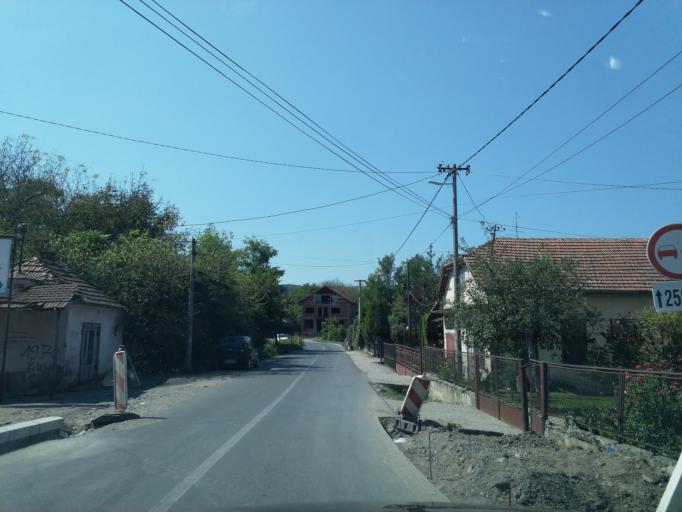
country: RS
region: Central Serbia
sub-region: Rasinski Okrug
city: Krusevac
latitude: 43.6155
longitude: 21.2979
